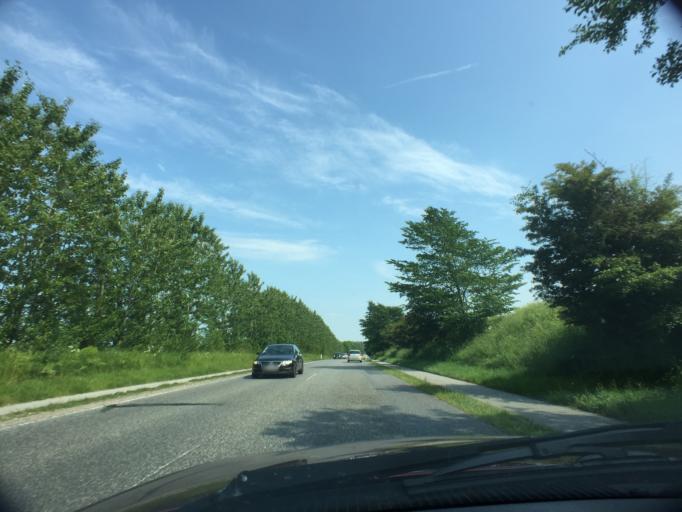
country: DK
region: Central Jutland
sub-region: Skanderborg Kommune
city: Skovby
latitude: 56.2283
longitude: 9.9503
